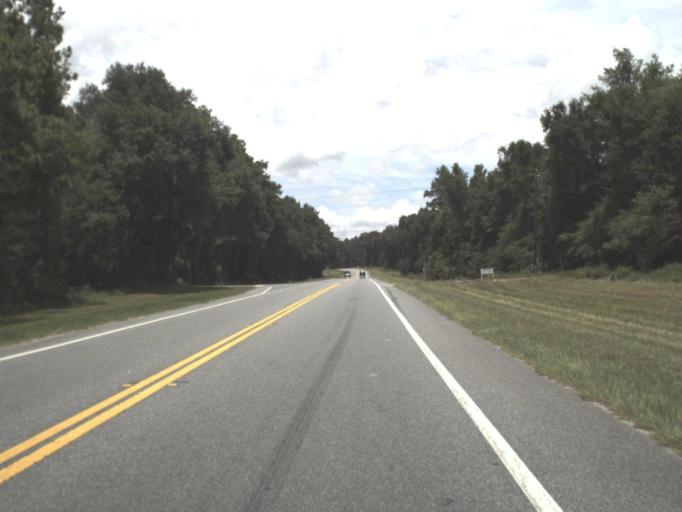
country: US
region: Florida
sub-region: Suwannee County
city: Live Oak
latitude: 30.3475
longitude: -82.9501
